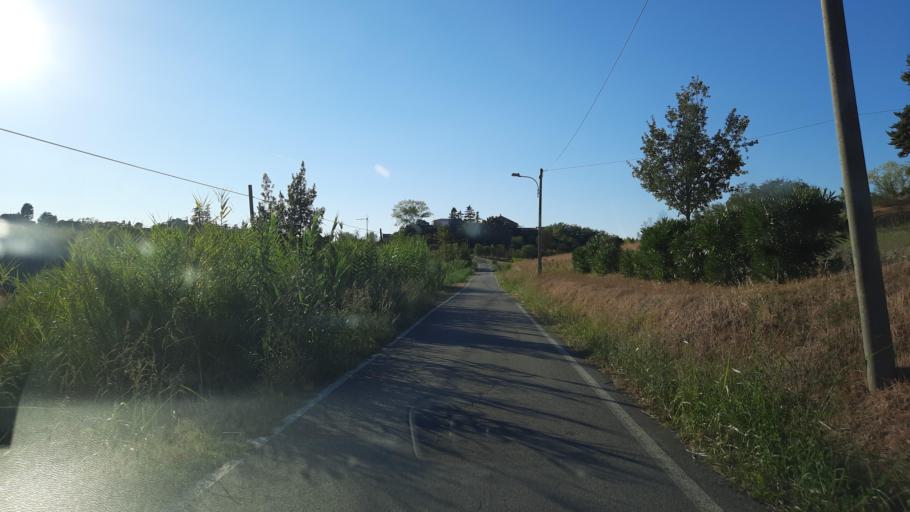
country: IT
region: Piedmont
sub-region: Provincia di Alessandria
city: Camagna Monferrato
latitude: 44.9998
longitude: 8.4270
